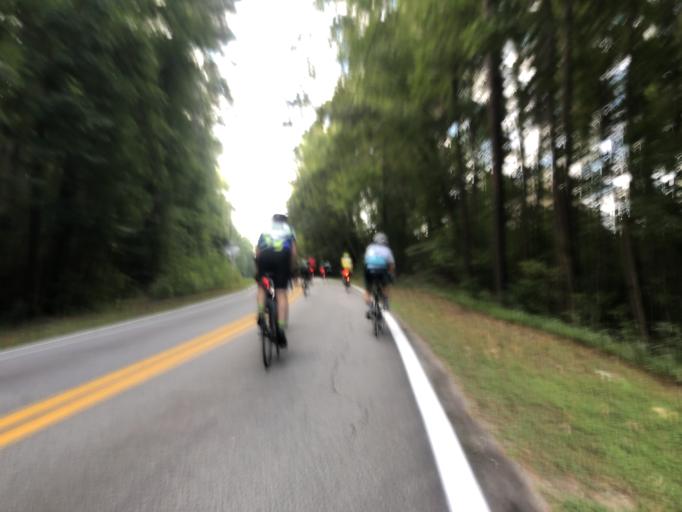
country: US
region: Georgia
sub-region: Fulton County
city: Palmetto
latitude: 33.5917
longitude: -84.6537
